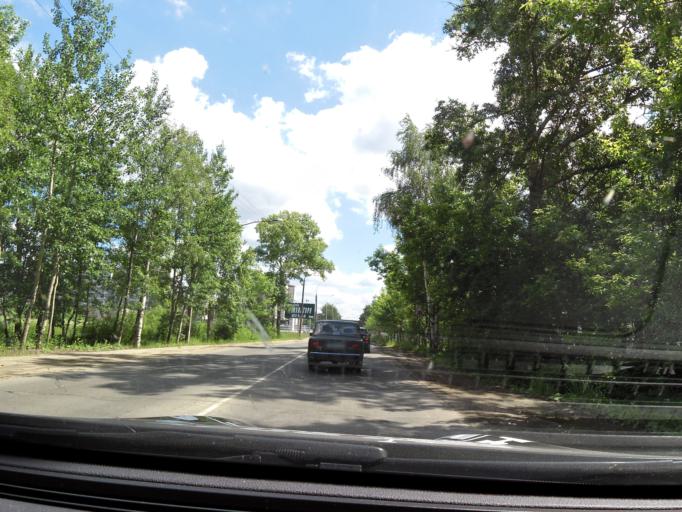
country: RU
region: Vologda
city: Vologda
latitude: 59.2277
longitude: 39.8581
